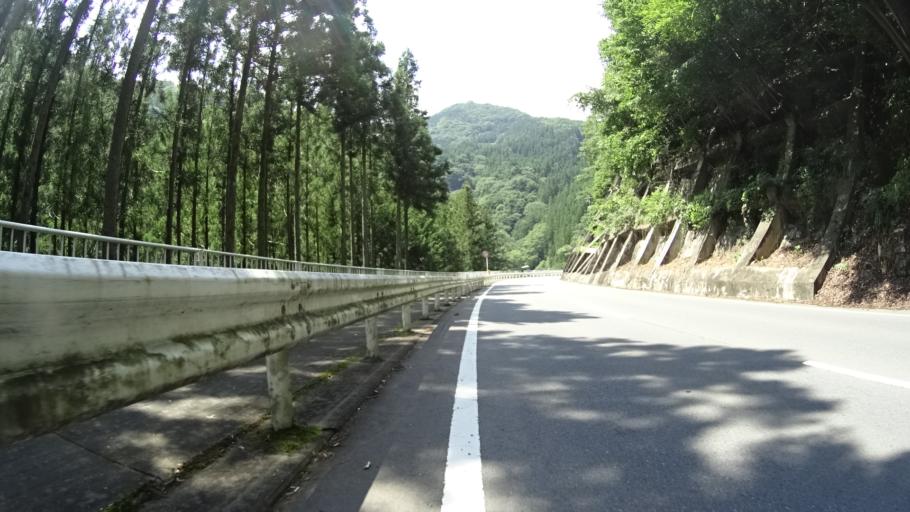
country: JP
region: Gunma
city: Tomioka
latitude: 36.0774
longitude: 138.7822
